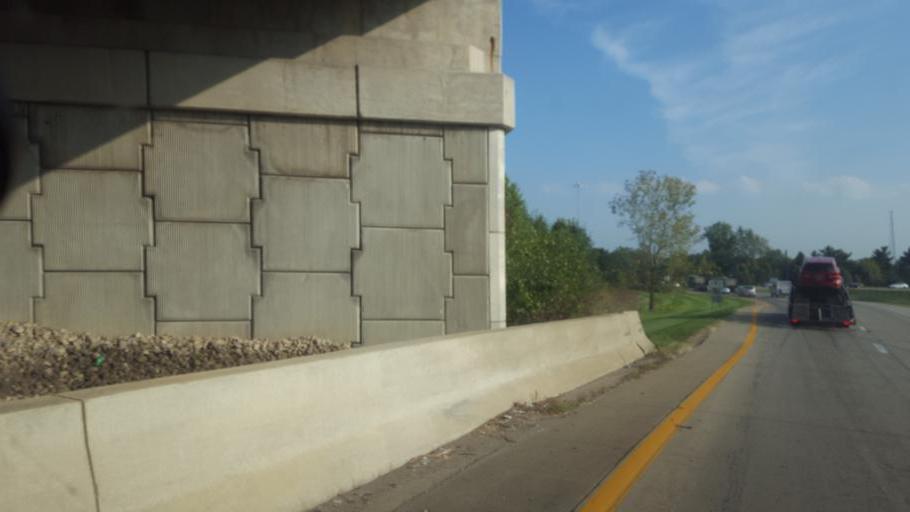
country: US
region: Ohio
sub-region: Franklin County
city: Huber Ridge
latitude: 40.0556
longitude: -82.9020
